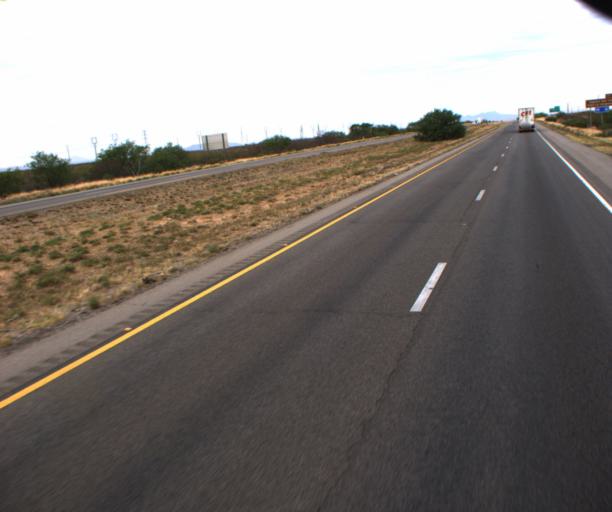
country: US
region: Arizona
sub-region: Pima County
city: Vail
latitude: 32.0532
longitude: -110.7602
